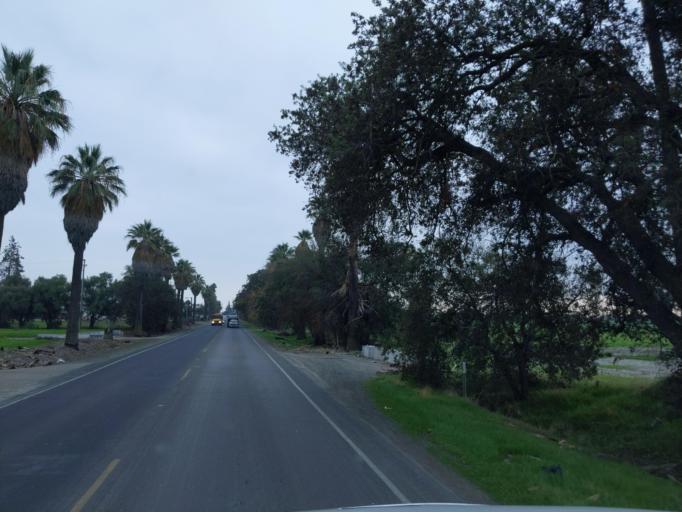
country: US
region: California
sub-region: San Joaquin County
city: August
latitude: 37.9948
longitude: -121.2579
